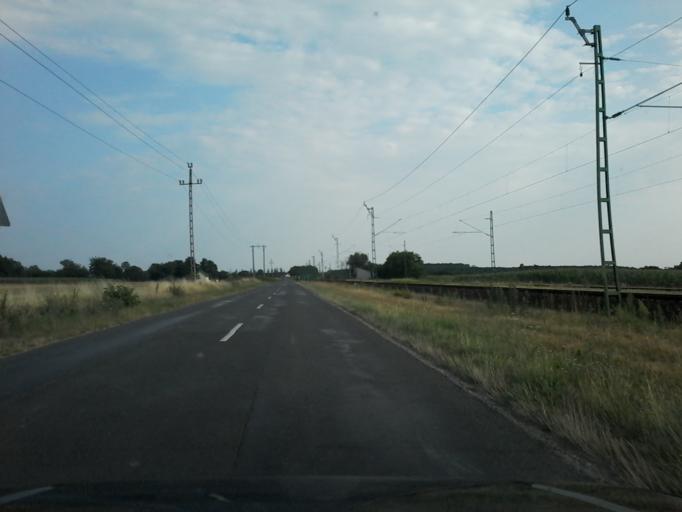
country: HU
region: Vas
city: Janoshaza
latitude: 47.0972
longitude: 17.1828
